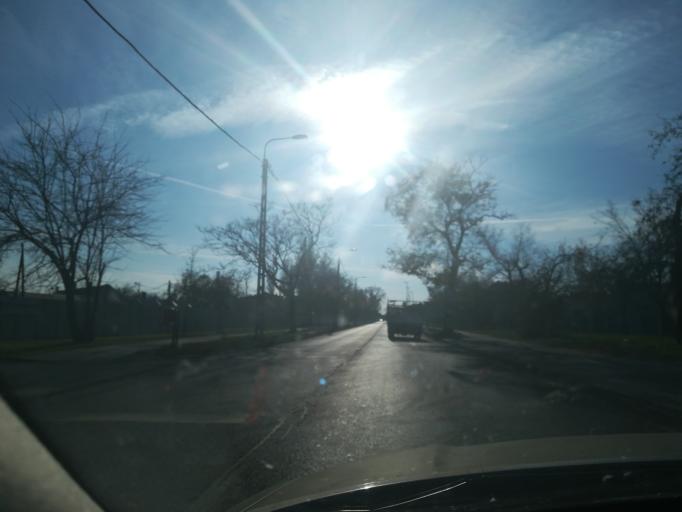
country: HU
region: Budapest
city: Budapest XX. keruelet
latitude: 47.4681
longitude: 19.1069
